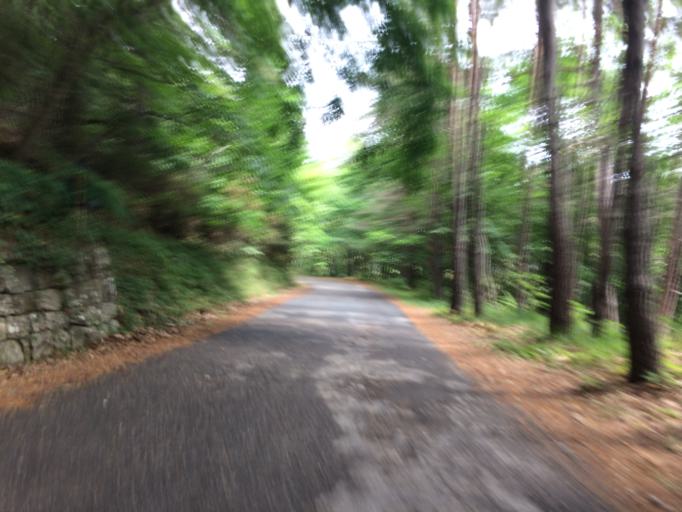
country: IT
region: Liguria
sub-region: Provincia di Imperia
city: Bajardo
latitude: 43.8892
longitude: 7.7342
